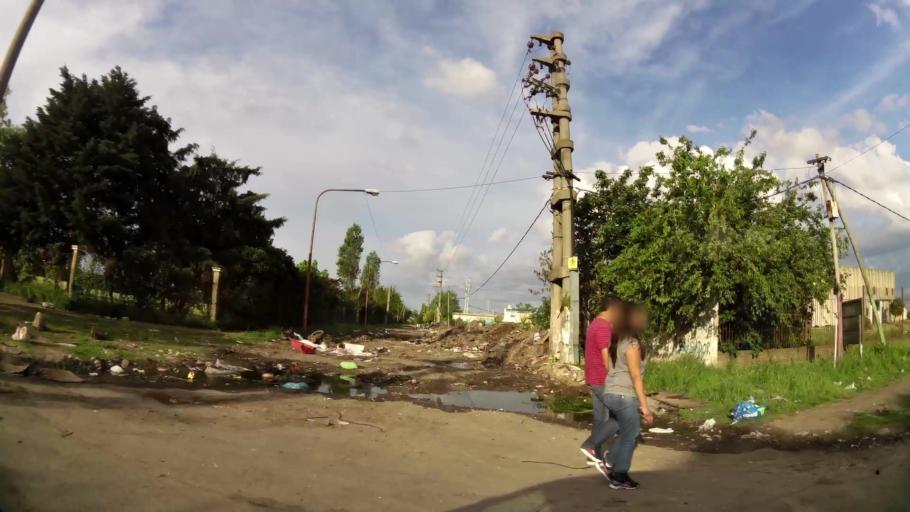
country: AR
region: Buenos Aires
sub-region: Partido de Quilmes
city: Quilmes
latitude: -34.7513
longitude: -58.2615
